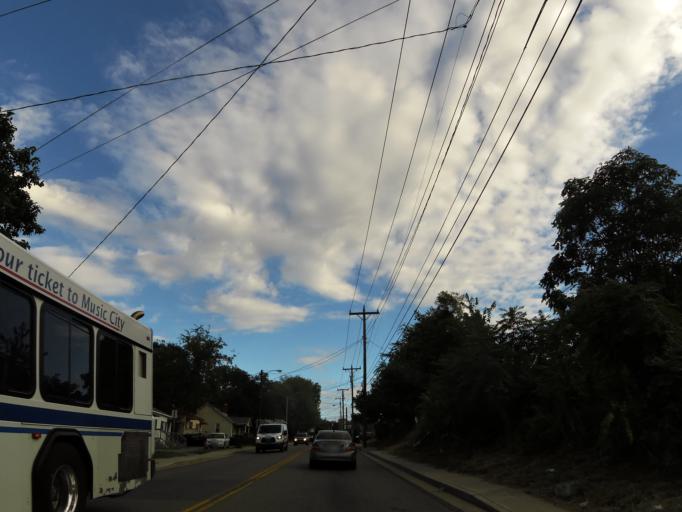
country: US
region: Tennessee
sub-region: Davidson County
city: Nashville
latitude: 36.1610
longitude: -86.8191
